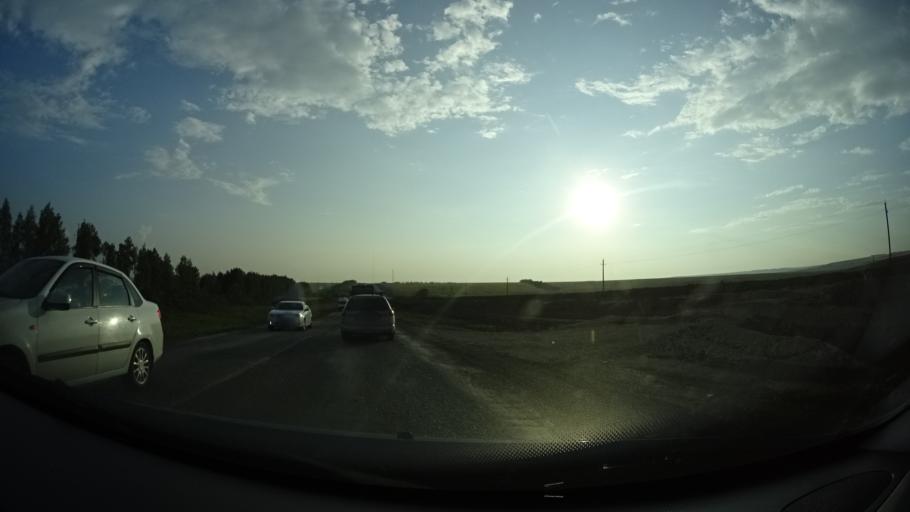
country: RU
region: Samara
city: Kamyshla
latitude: 54.0491
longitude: 52.0285
